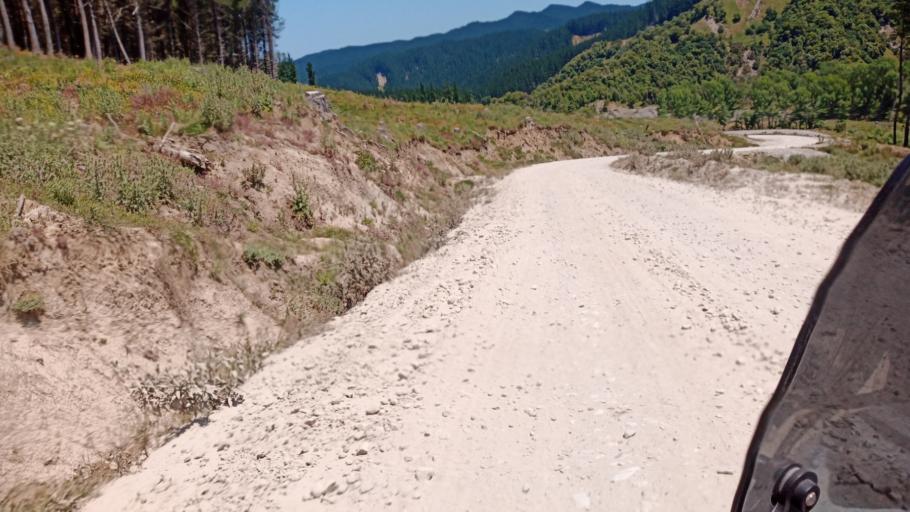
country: NZ
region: Gisborne
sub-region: Gisborne District
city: Gisborne
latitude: -38.2848
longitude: 178.0044
